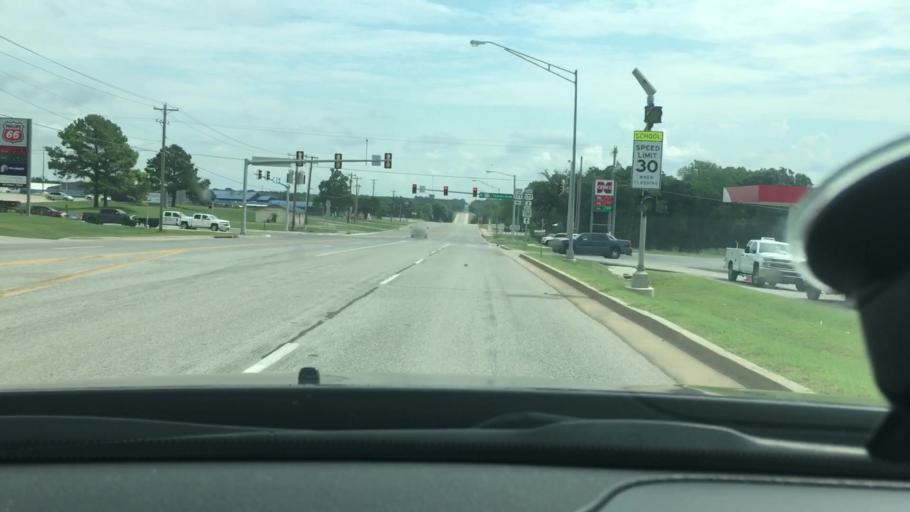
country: US
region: Oklahoma
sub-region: Carter County
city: Dickson
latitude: 34.1871
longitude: -96.9871
